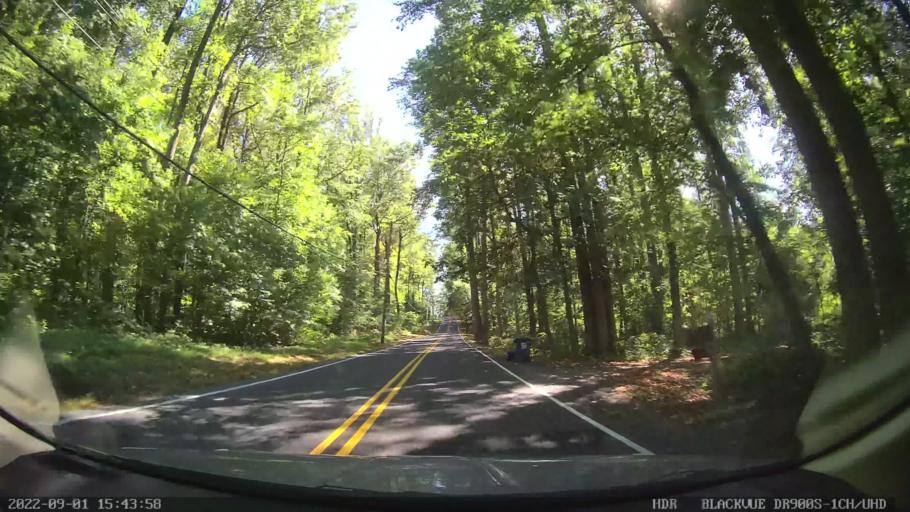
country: US
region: Pennsylvania
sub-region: Berks County
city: Topton
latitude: 40.4762
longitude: -75.6999
